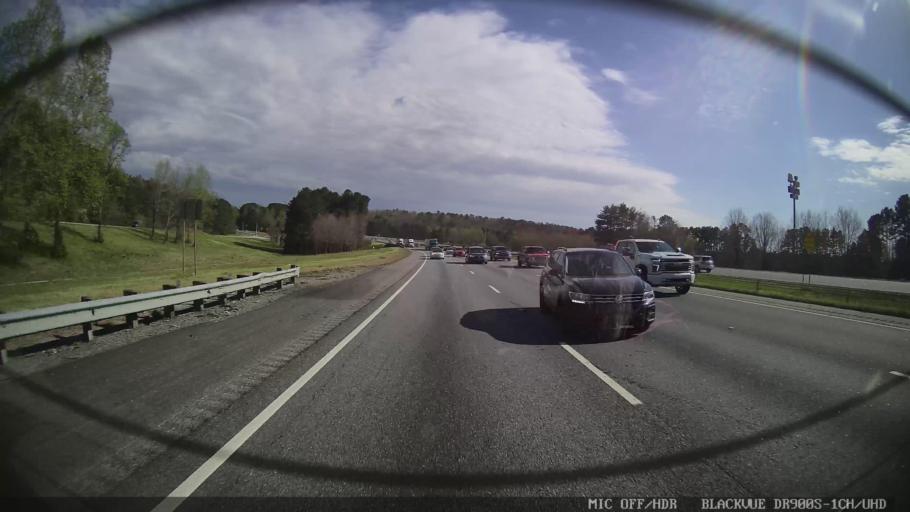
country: US
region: Georgia
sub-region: Bartow County
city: Emerson
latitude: 34.1218
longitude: -84.7400
